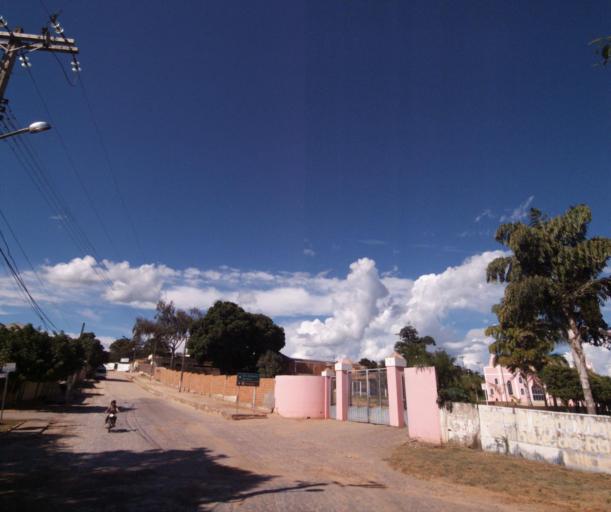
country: BR
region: Bahia
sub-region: Correntina
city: Correntina
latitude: -13.3402
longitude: -44.6362
